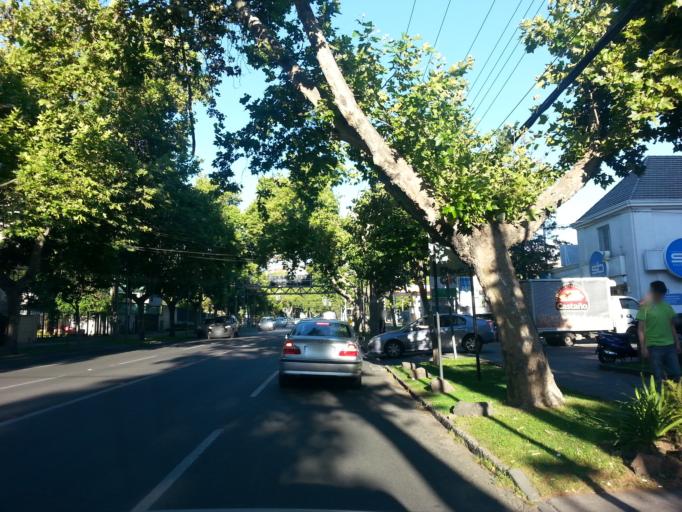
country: CL
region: Santiago Metropolitan
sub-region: Provincia de Santiago
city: Villa Presidente Frei, Nunoa, Santiago, Chile
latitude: -33.4238
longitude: -70.5805
